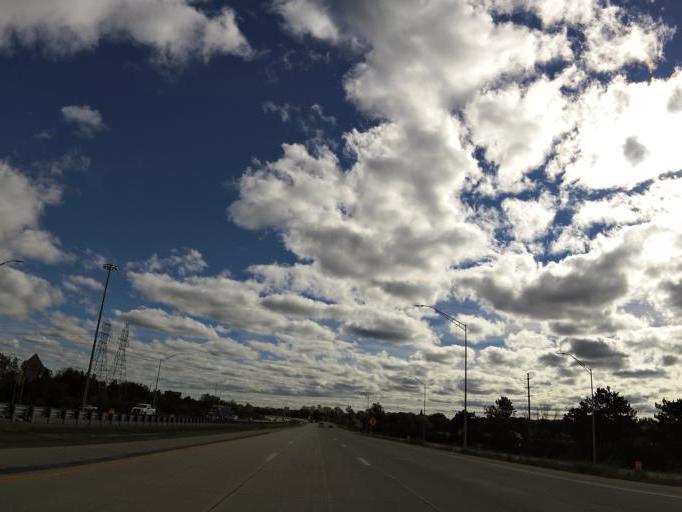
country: US
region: Michigan
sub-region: Genesee County
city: Burton
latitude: 43.0138
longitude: -83.6328
